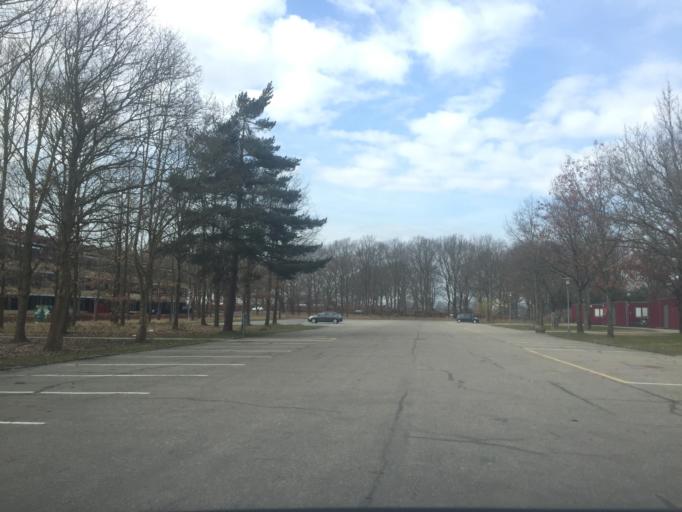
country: DK
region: Capital Region
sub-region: Lyngby-Tarbaek Kommune
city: Kongens Lyngby
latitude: 55.7836
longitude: 12.5151
